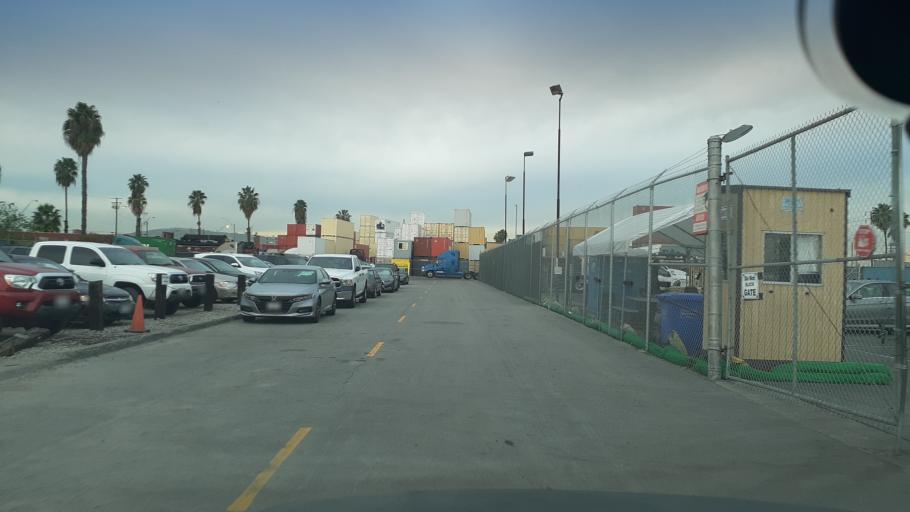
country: US
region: California
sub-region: Los Angeles County
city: Long Beach
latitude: 33.7819
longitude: -118.2161
